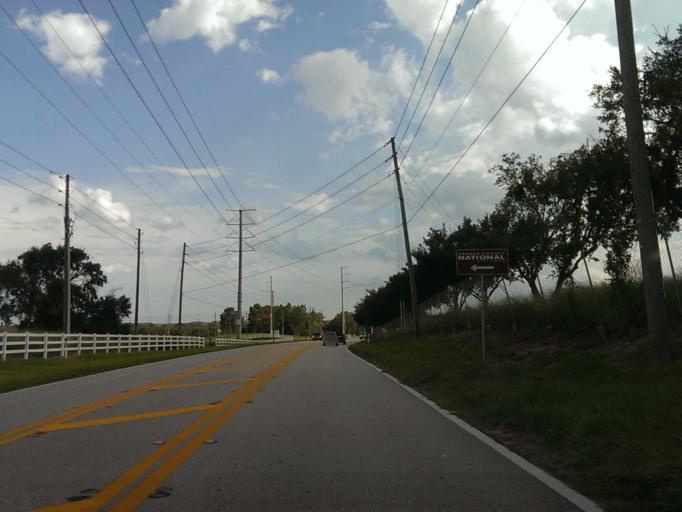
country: US
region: Florida
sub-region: Polk County
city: Citrus Ridge
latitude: 28.4439
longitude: -81.6362
